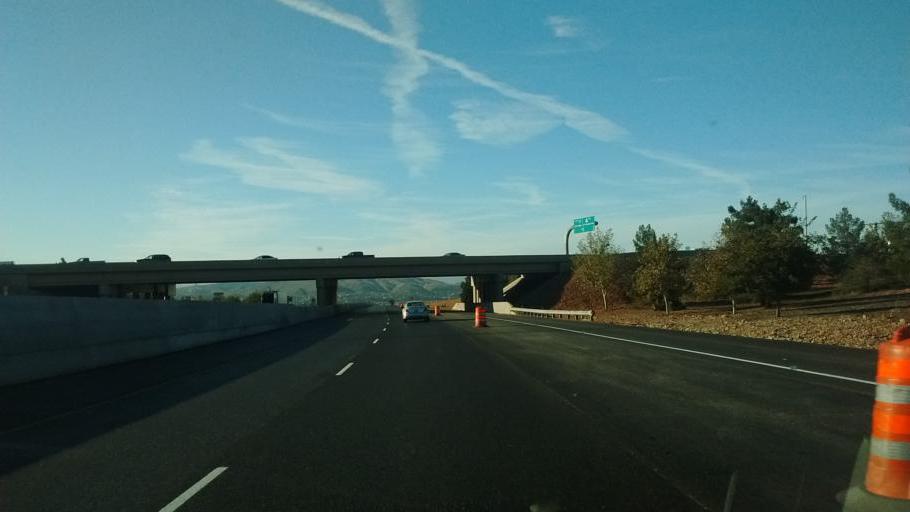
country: US
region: Utah
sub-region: Washington County
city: Saint George
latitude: 37.1109
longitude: -113.5577
